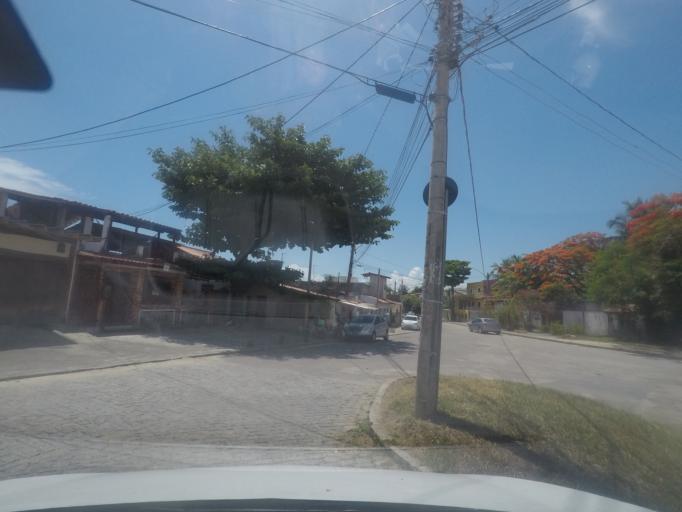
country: BR
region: Rio de Janeiro
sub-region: Itaguai
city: Itaguai
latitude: -23.0058
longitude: -43.6346
